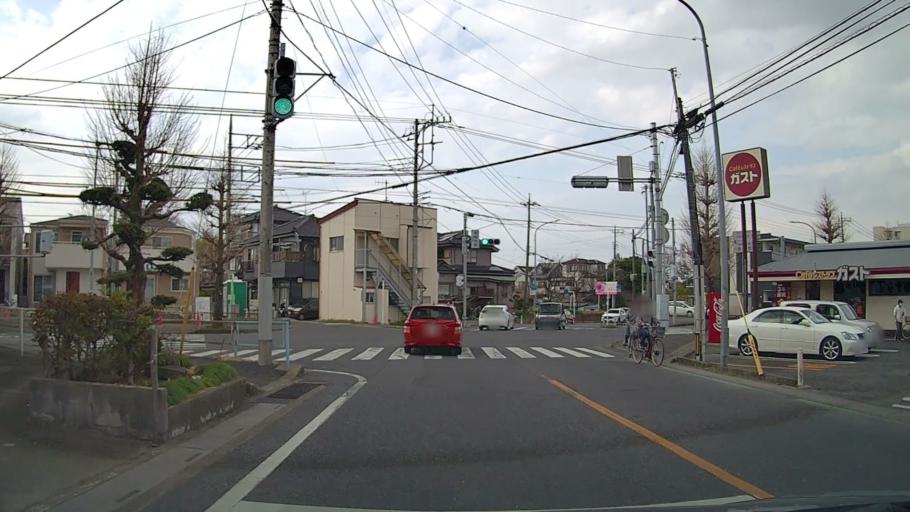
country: JP
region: Saitama
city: Asaka
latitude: 35.8096
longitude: 139.5983
